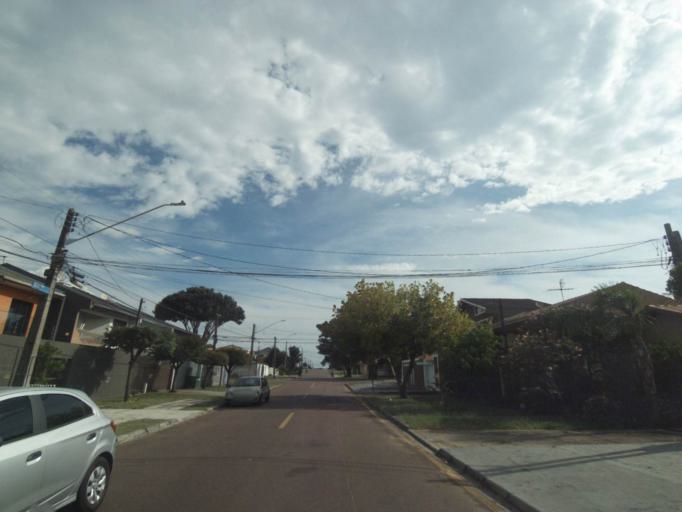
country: BR
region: Parana
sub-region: Pinhais
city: Pinhais
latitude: -25.4432
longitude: -49.2206
